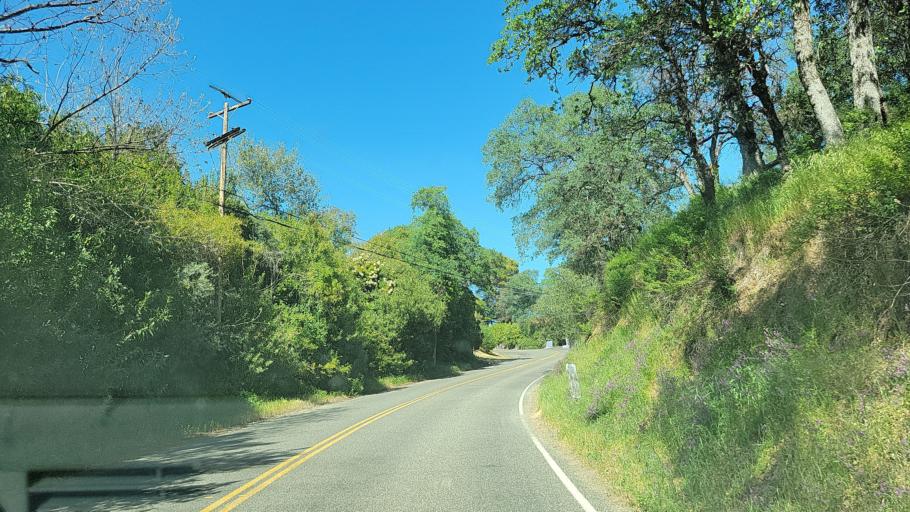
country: US
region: California
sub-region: Tehama County
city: Red Bluff
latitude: 40.1974
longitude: -122.2254
